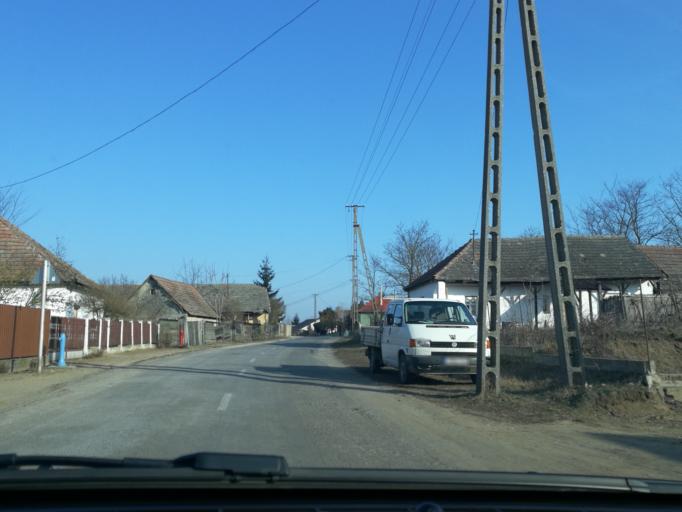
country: HU
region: Szabolcs-Szatmar-Bereg
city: Nyirbogdany
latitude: 48.0553
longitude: 21.9355
